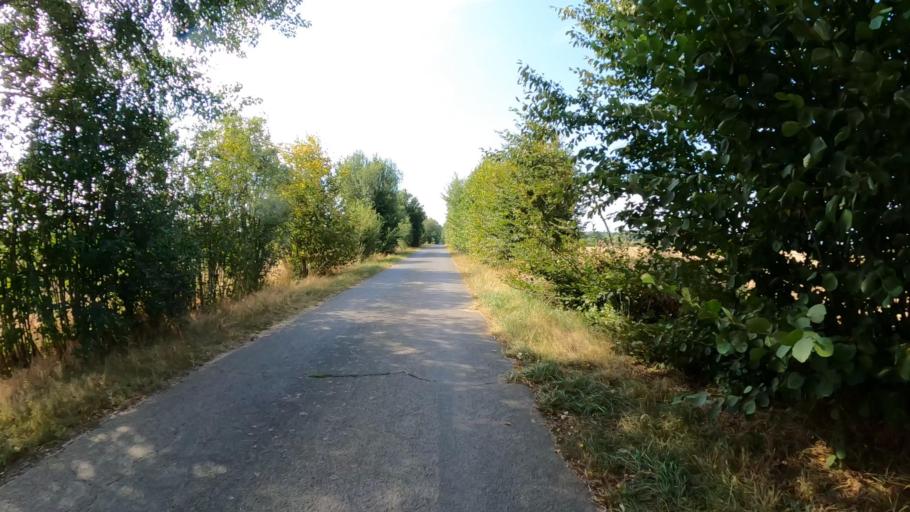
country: DE
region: Schleswig-Holstein
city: Hamwarde
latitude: 53.4563
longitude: 10.4083
